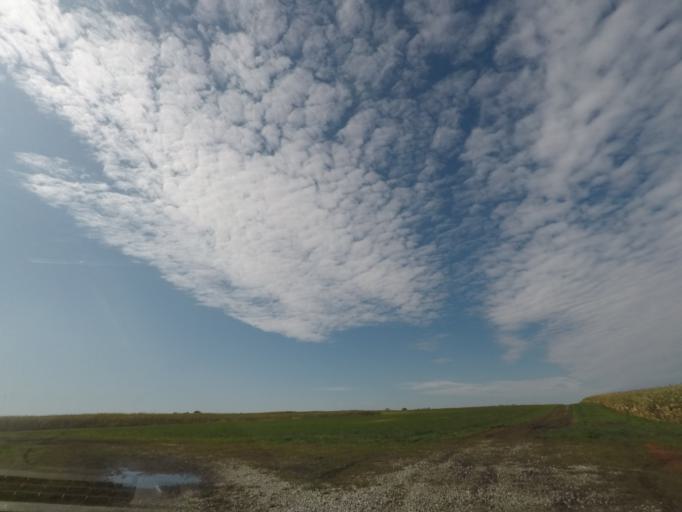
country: US
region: Iowa
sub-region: Boone County
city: Boone
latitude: 42.0160
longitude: -93.7816
